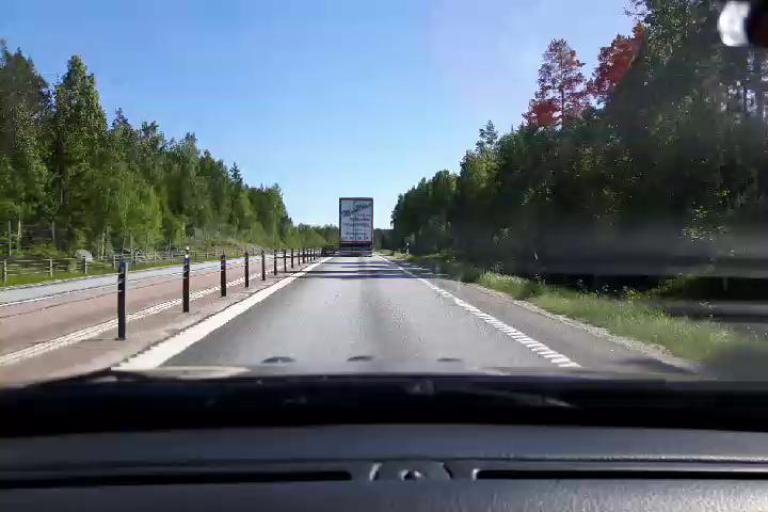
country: SE
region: Gaevleborg
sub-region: Soderhamns Kommun
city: Soderhamn
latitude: 61.2623
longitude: 17.0323
